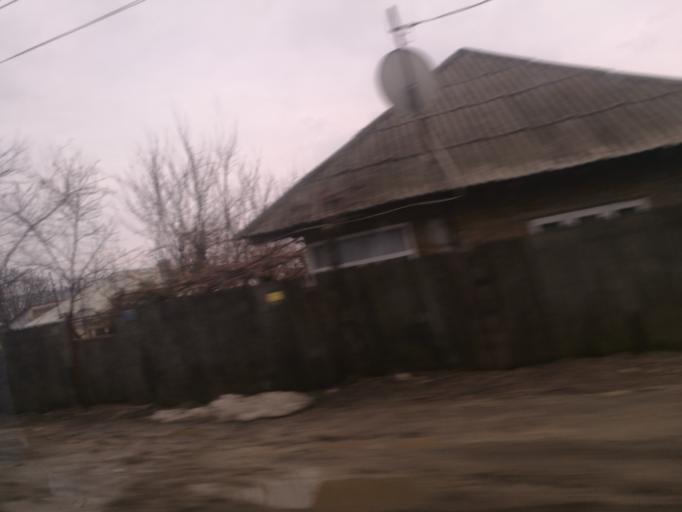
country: RO
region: Iasi
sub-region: Comuna Targu Frumos
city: Targu Frumos
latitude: 47.2041
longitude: 27.0016
